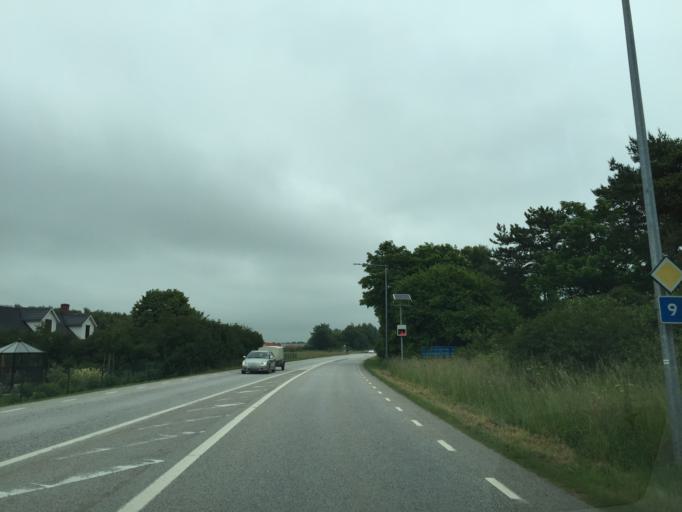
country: SE
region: Skane
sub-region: Ystads Kommun
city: Kopingebro
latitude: 55.4348
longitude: 13.9306
